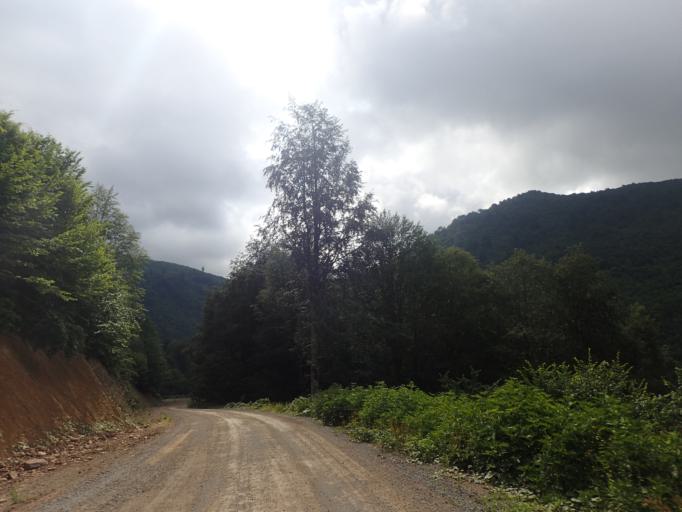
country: TR
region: Ordu
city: Akkus
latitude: 40.8594
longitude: 37.0010
